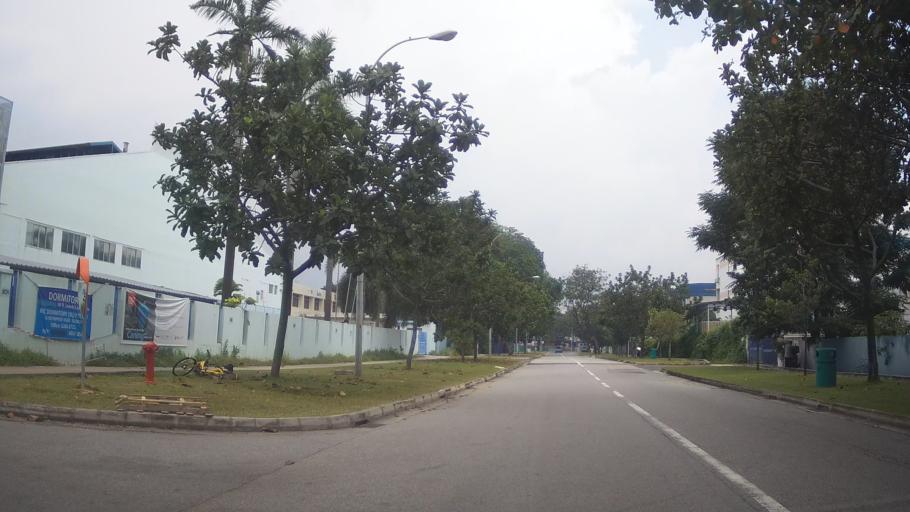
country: MY
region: Johor
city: Johor Bahru
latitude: 1.3333
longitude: 103.7042
